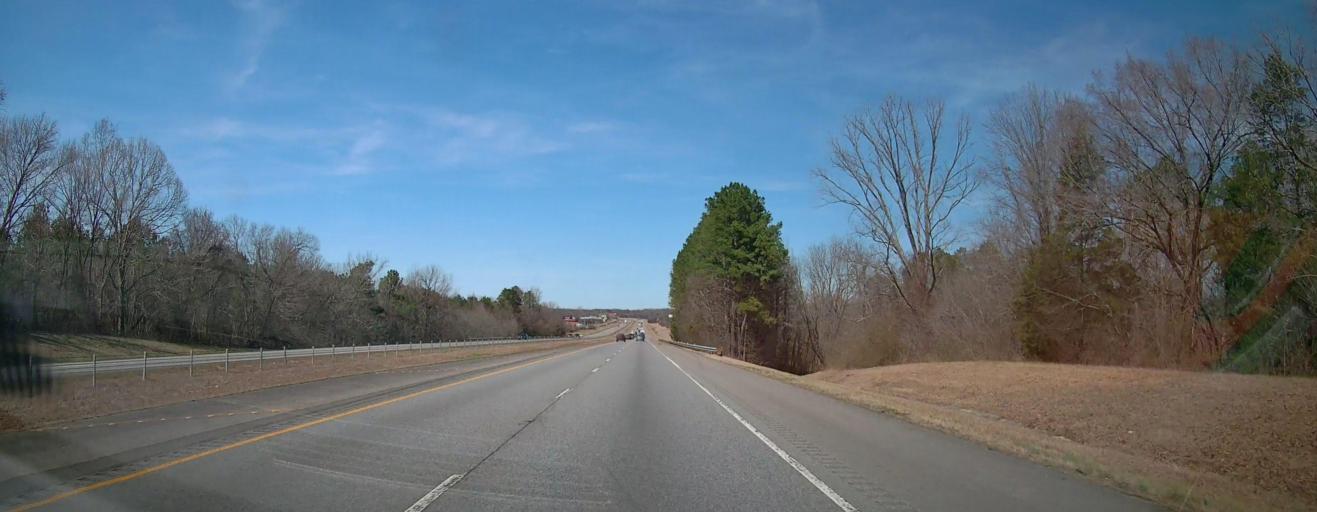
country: US
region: Alabama
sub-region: Morgan County
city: Priceville
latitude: 34.4863
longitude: -86.8981
